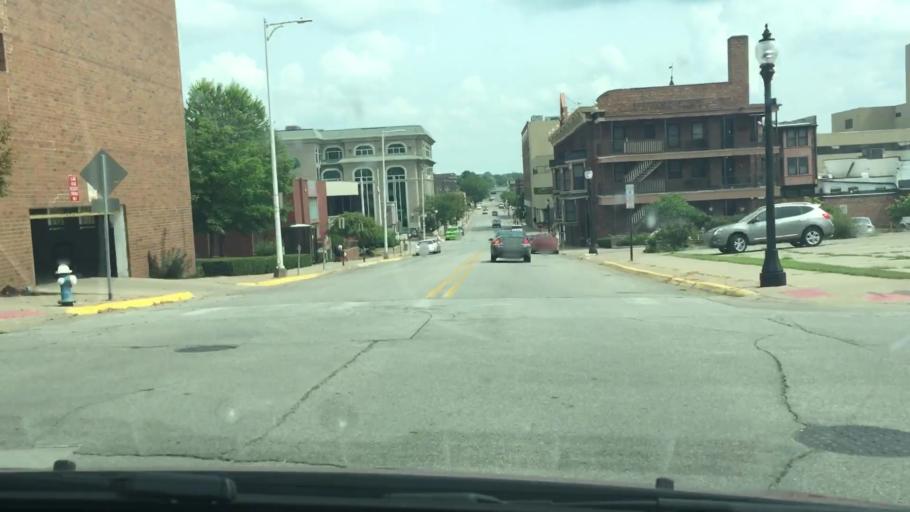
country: US
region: Iowa
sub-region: Muscatine County
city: Muscatine
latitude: 41.4215
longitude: -91.0476
